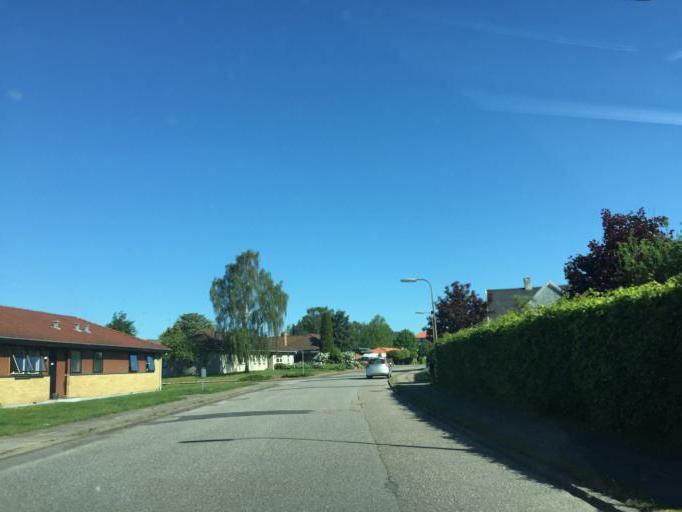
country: DK
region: South Denmark
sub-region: Odense Kommune
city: Odense
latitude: 55.3549
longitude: 10.3869
